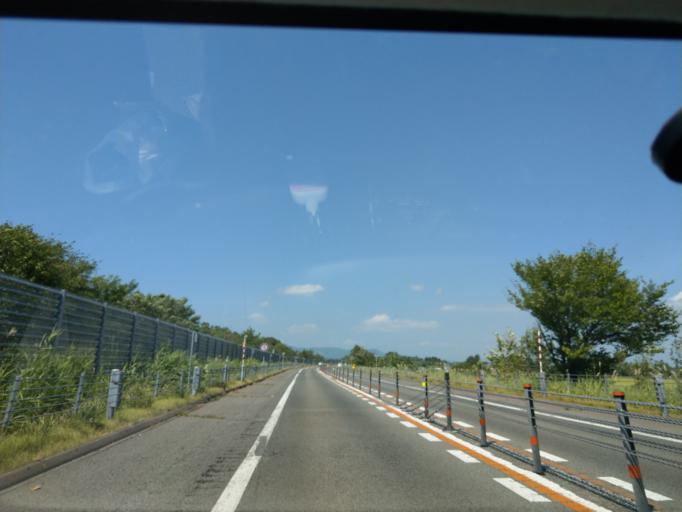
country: JP
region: Akita
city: Yokotemachi
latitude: 39.3451
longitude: 140.4994
